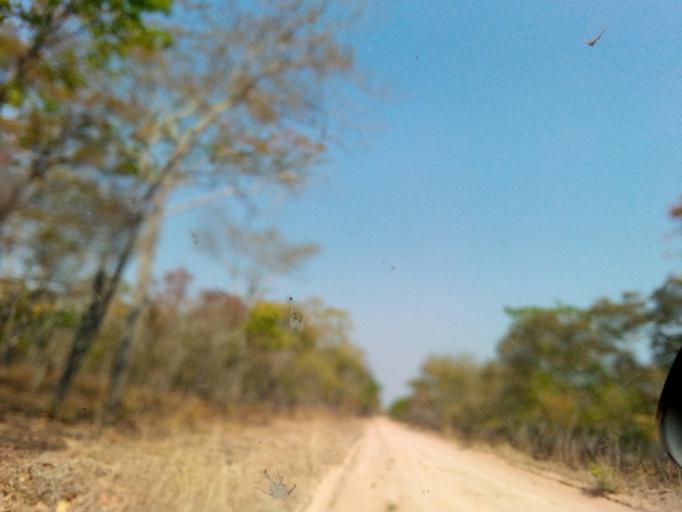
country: ZM
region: Northern
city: Mpika
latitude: -12.2422
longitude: 30.8414
